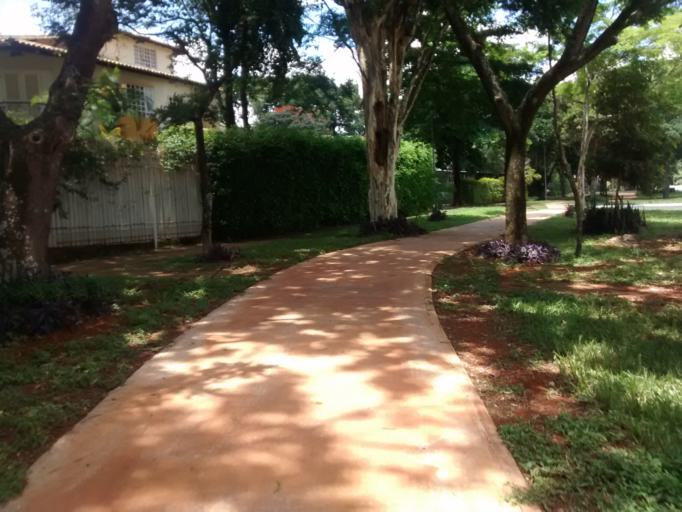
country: BR
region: Federal District
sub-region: Brasilia
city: Brasilia
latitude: -15.8202
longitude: -47.9216
